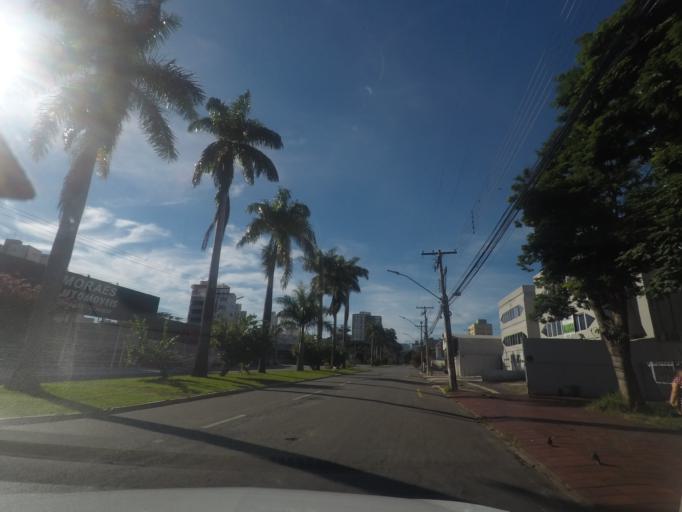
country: BR
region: Goias
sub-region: Goiania
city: Goiania
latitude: -16.6730
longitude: -49.2693
